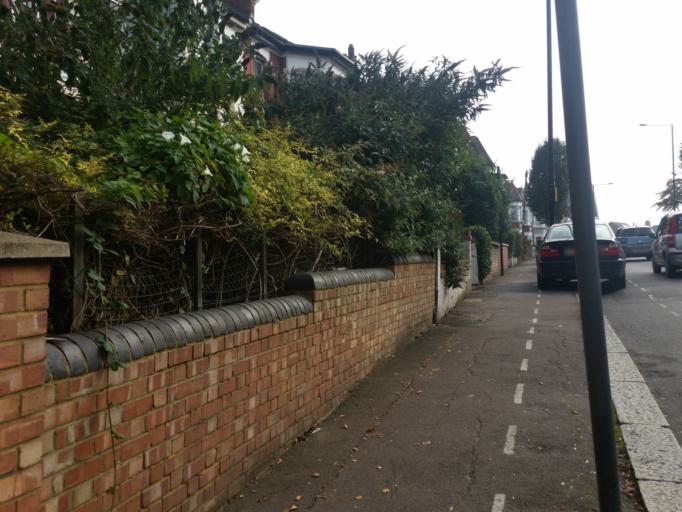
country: GB
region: England
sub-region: Greater London
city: Harringay
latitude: 51.5796
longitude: -0.1050
